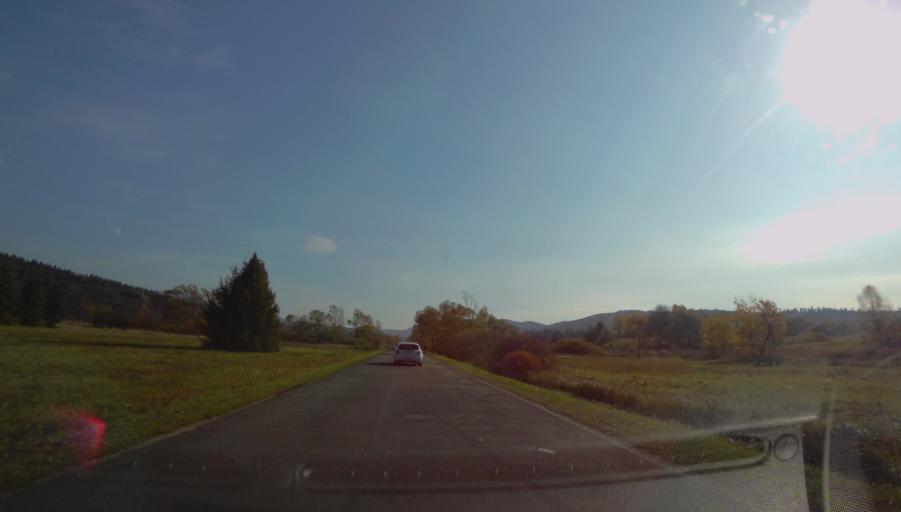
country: PL
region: Subcarpathian Voivodeship
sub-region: Powiat sanocki
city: Komancza
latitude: 49.2342
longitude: 22.1502
